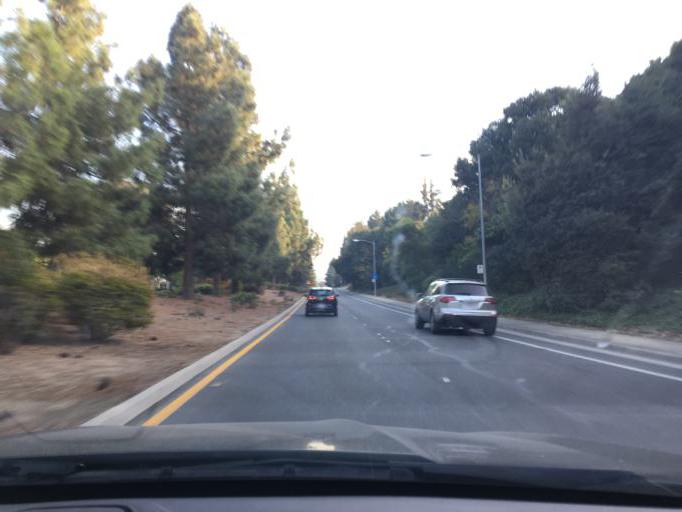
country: US
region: California
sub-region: Santa Clara County
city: Cupertino
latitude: 37.3281
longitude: -122.0693
